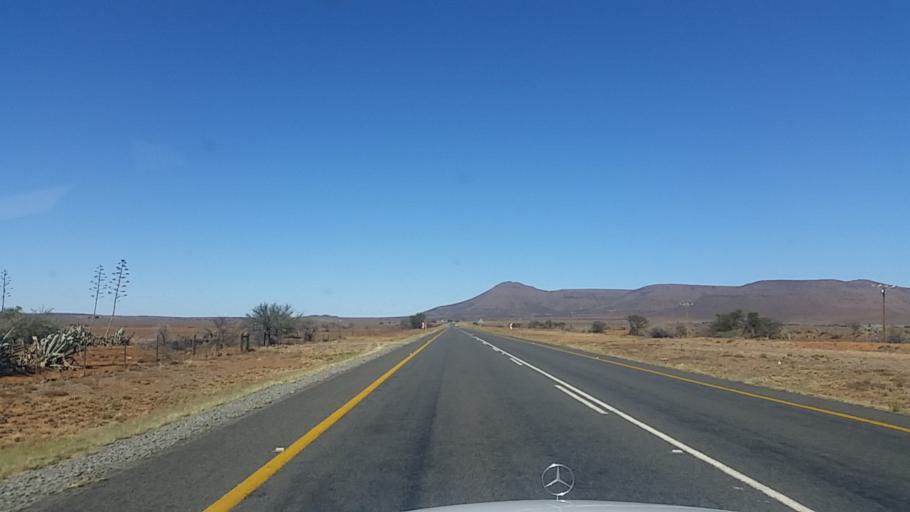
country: ZA
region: Eastern Cape
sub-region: Cacadu District Municipality
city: Graaff-Reinet
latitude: -32.0126
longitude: 24.6499
